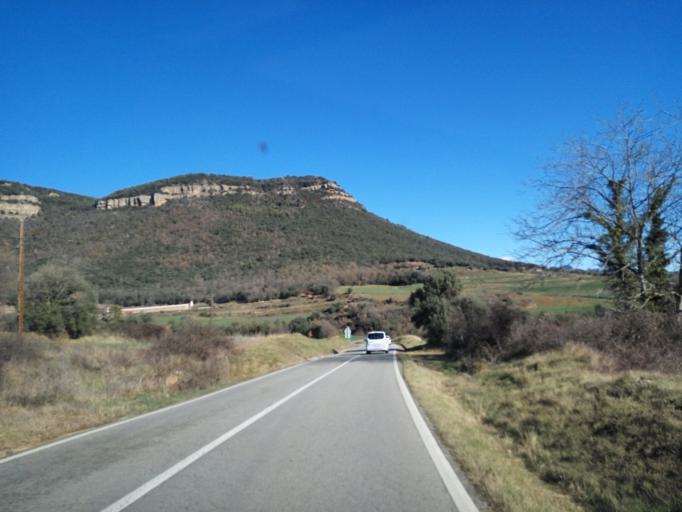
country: ES
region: Catalonia
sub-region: Provincia de Barcelona
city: Capolat
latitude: 42.0641
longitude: 1.7948
